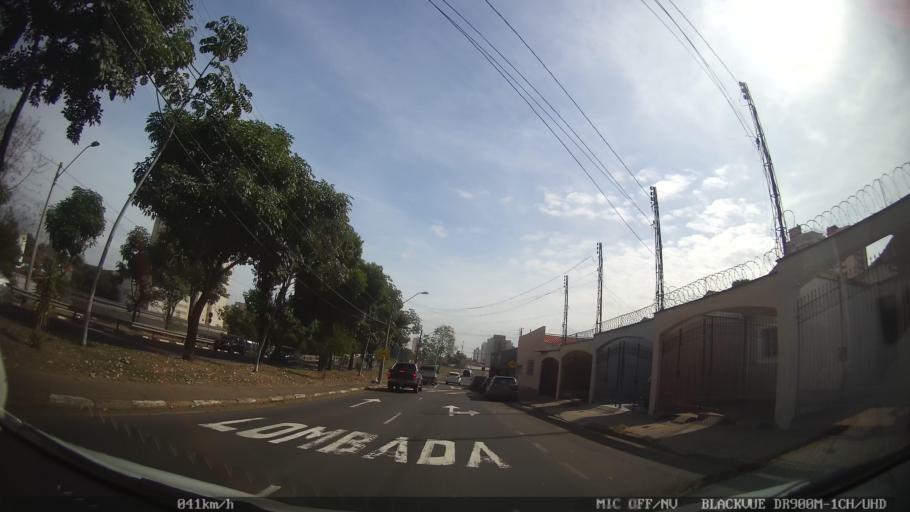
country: BR
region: Sao Paulo
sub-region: Piracicaba
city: Piracicaba
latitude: -22.7399
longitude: -47.6456
